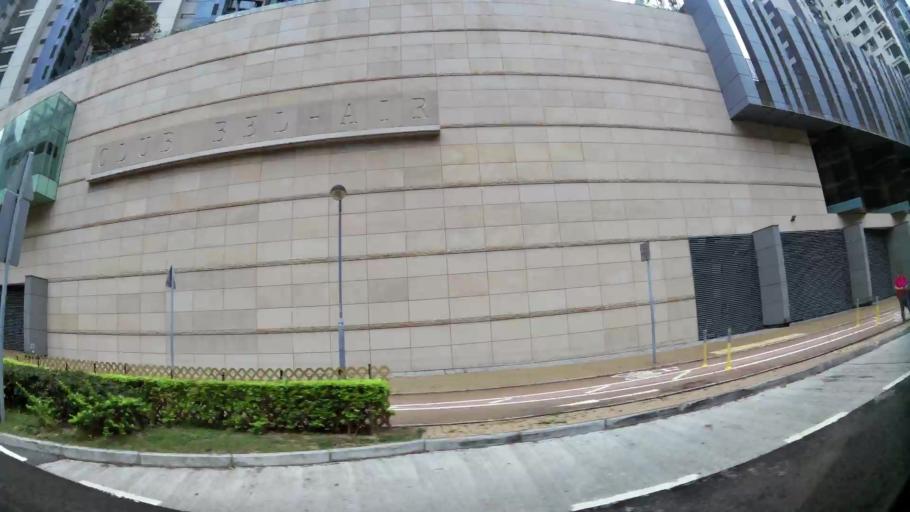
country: HK
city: Yung Shue Wan
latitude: 22.2567
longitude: 114.1325
